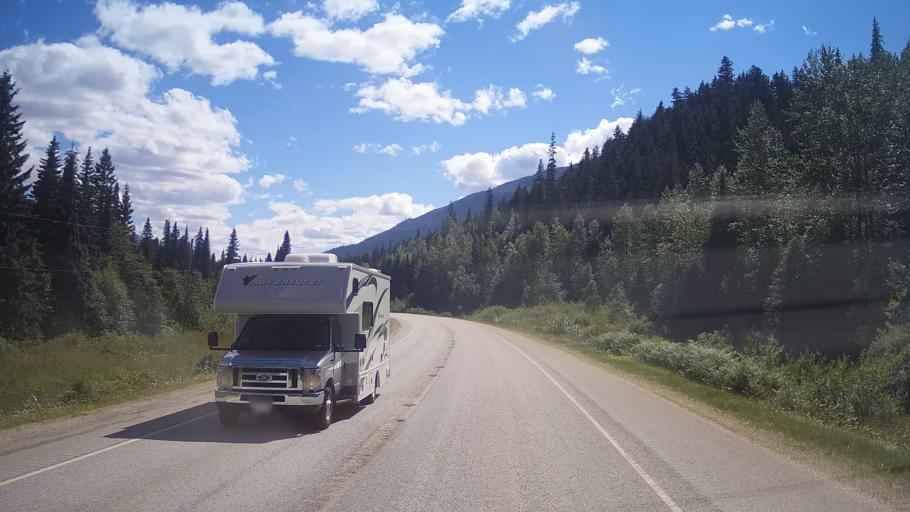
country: CA
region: Alberta
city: Jasper Park Lodge
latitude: 52.5634
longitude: -119.1080
